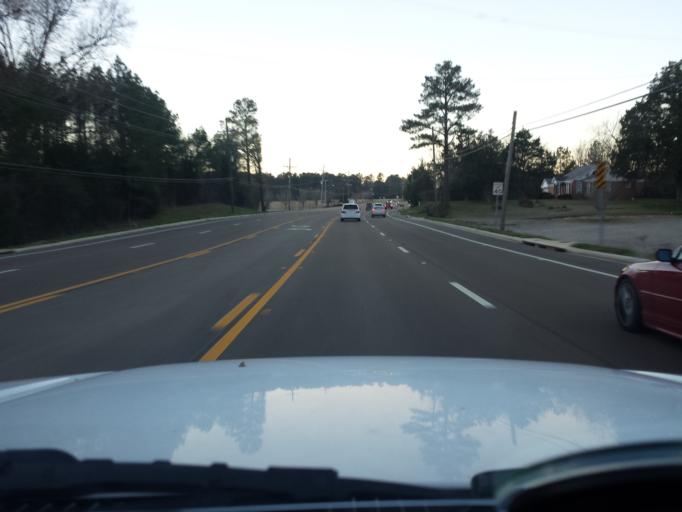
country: US
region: Mississippi
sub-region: Rankin County
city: Flowood
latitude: 32.3613
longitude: -90.0572
